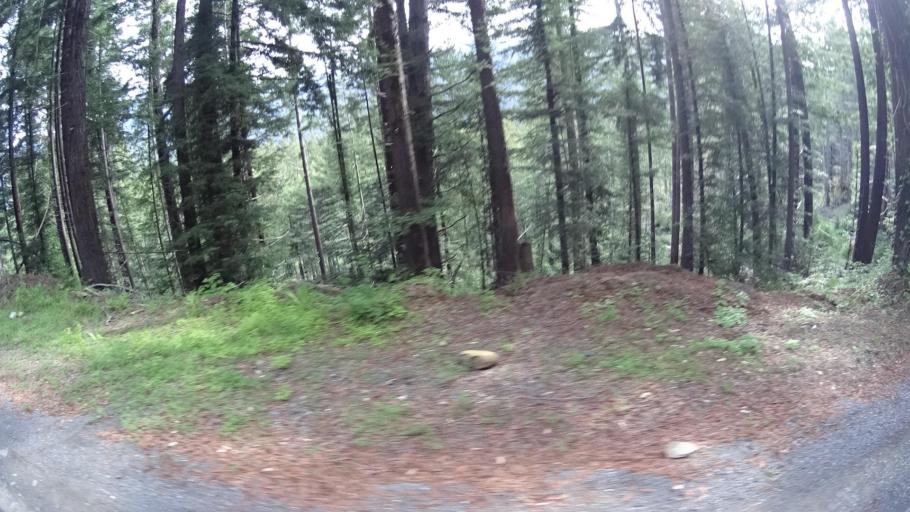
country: US
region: California
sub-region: Humboldt County
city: Redway
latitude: 40.3365
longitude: -123.8596
